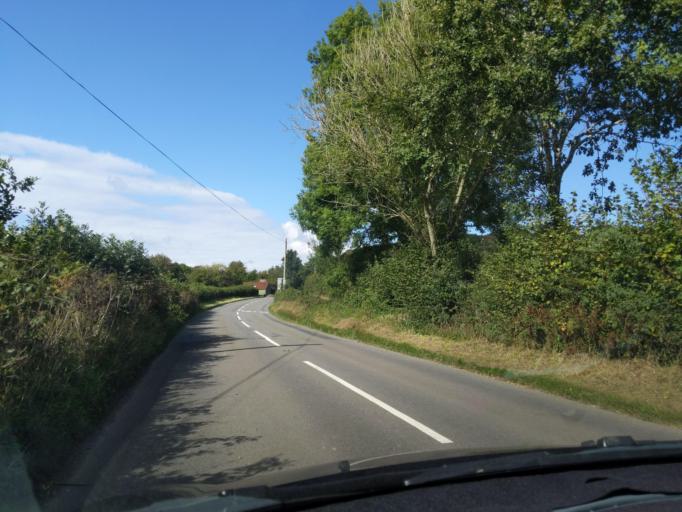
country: GB
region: England
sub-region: Cornwall
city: Werrington
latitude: 50.6978
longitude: -4.3221
